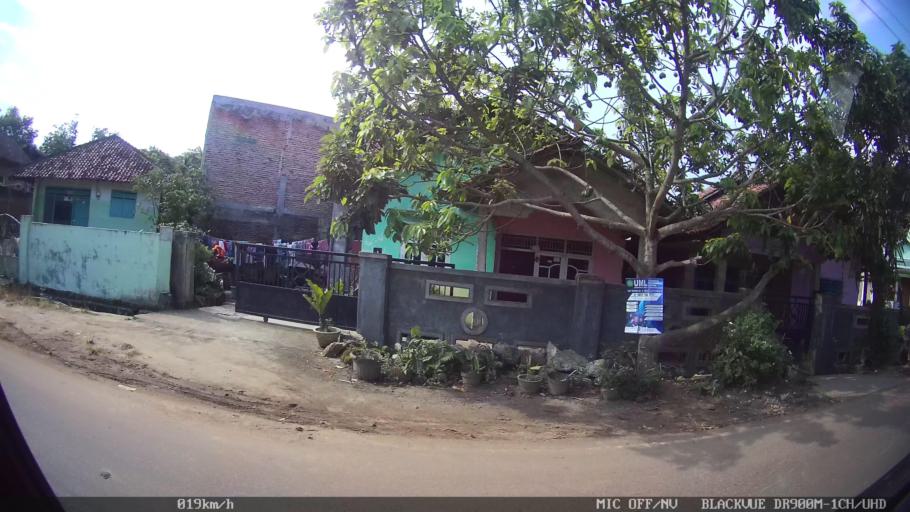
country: ID
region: Lampung
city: Bandarlampung
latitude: -5.4061
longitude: 105.2287
